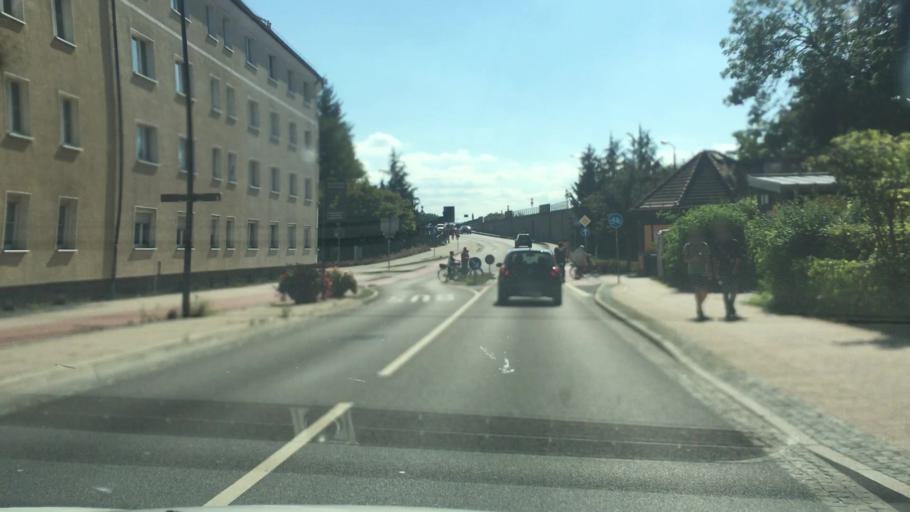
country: DE
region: Saxony
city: Pirna
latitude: 50.9680
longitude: 13.9345
